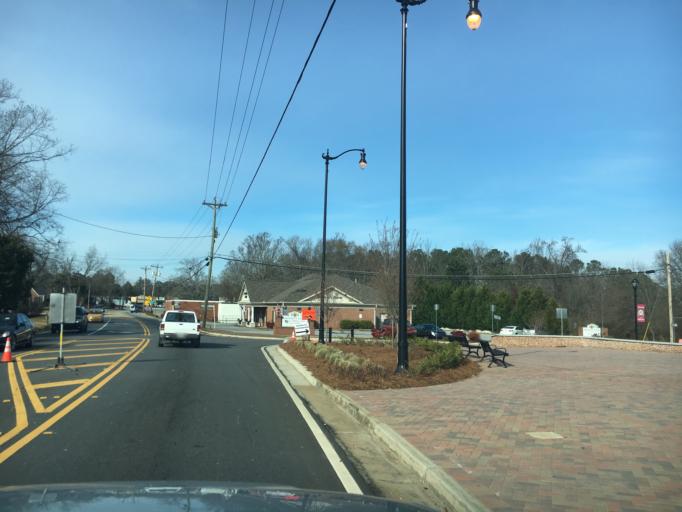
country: US
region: Georgia
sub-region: Jackson County
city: Braselton
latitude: 34.1093
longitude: -83.7628
